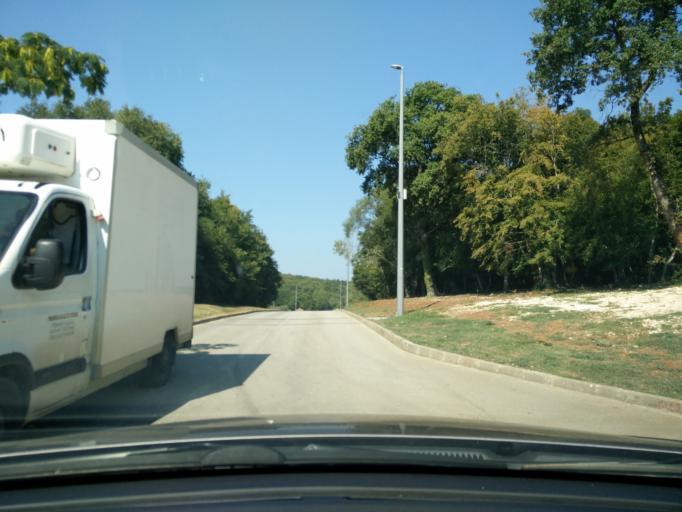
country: HR
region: Istarska
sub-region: Grad Porec
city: Porec
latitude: 45.1925
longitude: 13.5970
